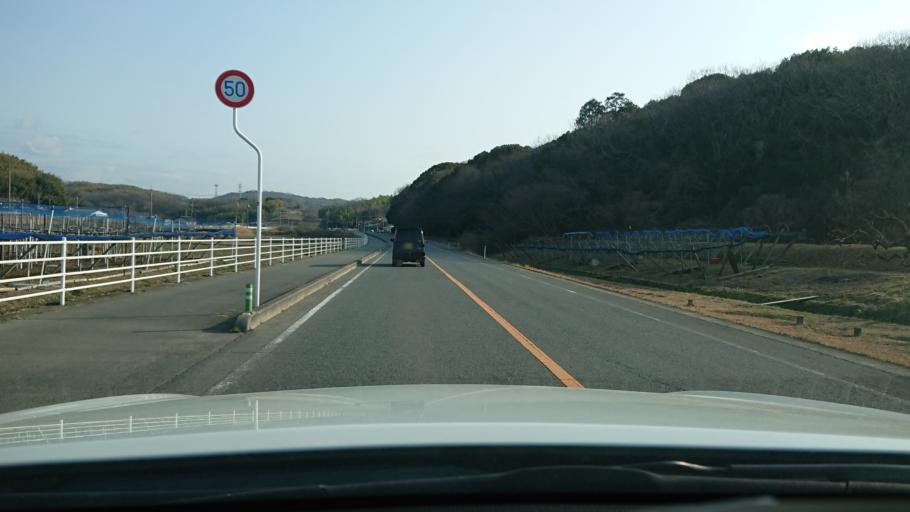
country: JP
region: Okayama
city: Kurashiki
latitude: 34.6048
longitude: 133.7059
